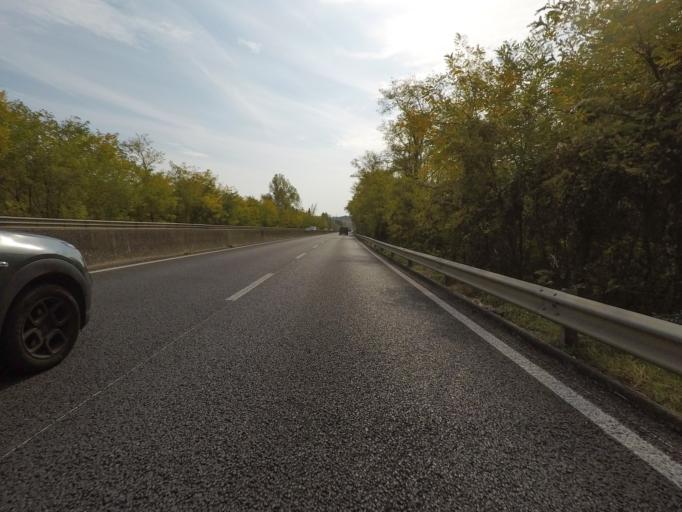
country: IT
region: Tuscany
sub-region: Provincia di Siena
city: Belverde
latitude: 43.3266
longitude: 11.2958
